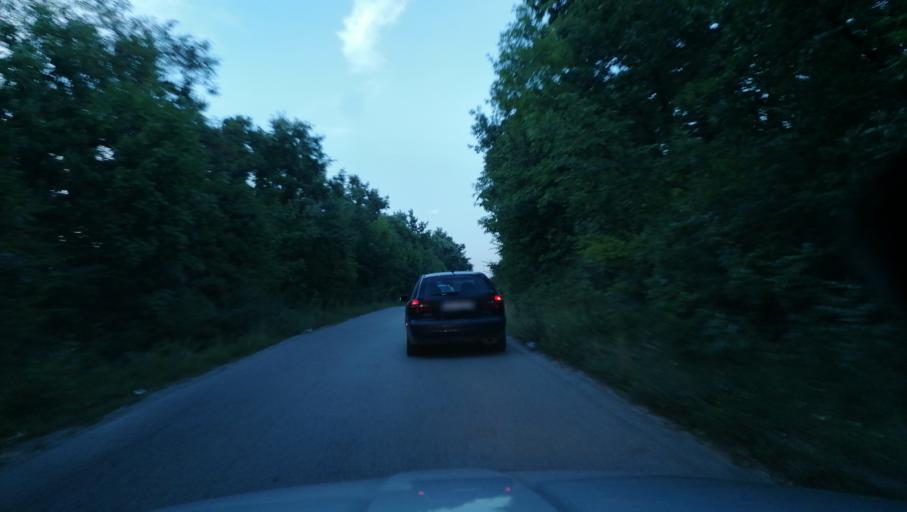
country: RS
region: Central Serbia
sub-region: Kolubarski Okrug
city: Valjevo
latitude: 44.2404
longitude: 19.8608
